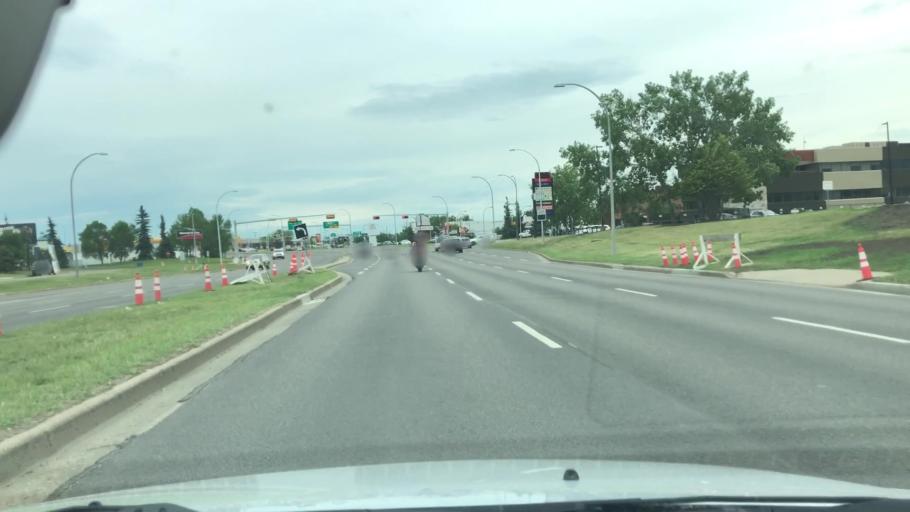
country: CA
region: Alberta
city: St. Albert
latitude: 53.5465
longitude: -113.6156
